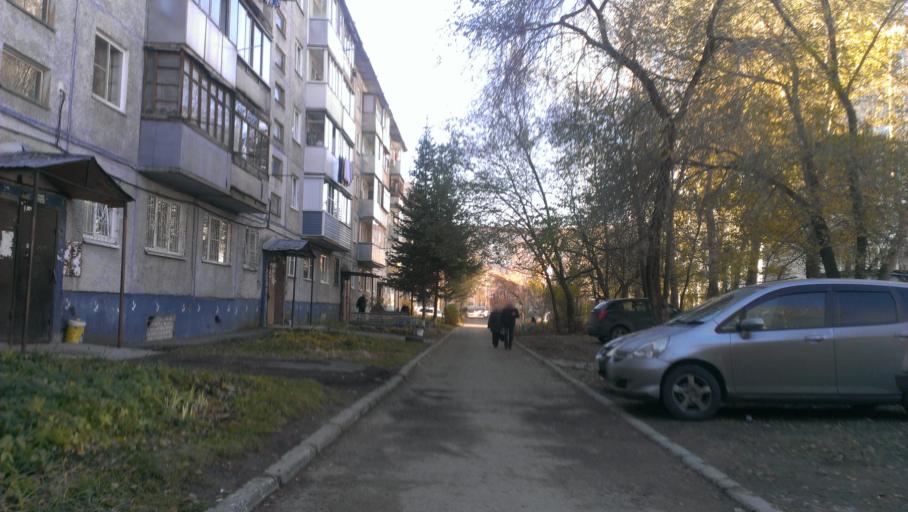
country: RU
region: Altai Krai
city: Novosilikatnyy
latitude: 53.3486
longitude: 83.6802
